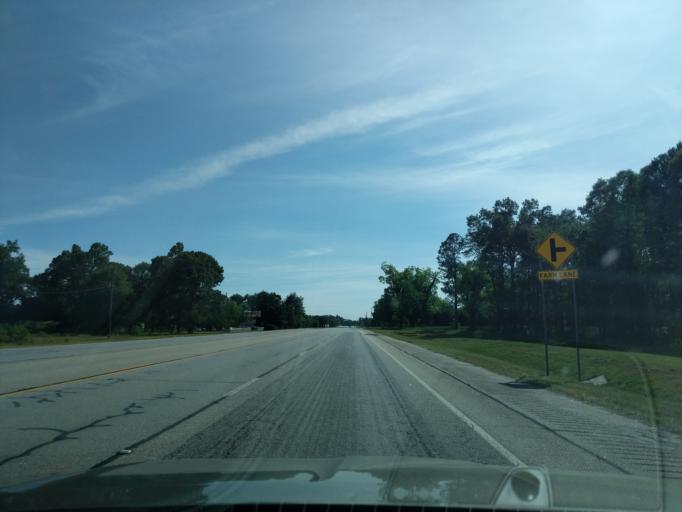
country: US
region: Georgia
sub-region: Jefferson County
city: Wrens
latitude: 33.2238
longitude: -82.3686
